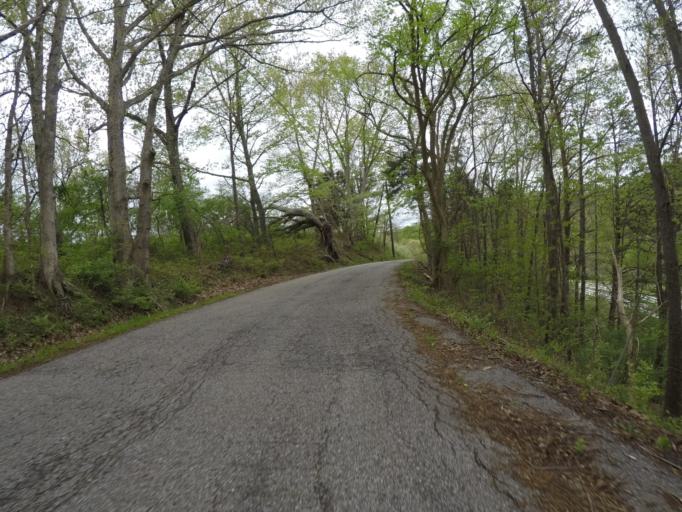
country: US
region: West Virginia
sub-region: Cabell County
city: Barboursville
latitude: 38.3928
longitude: -82.2505
